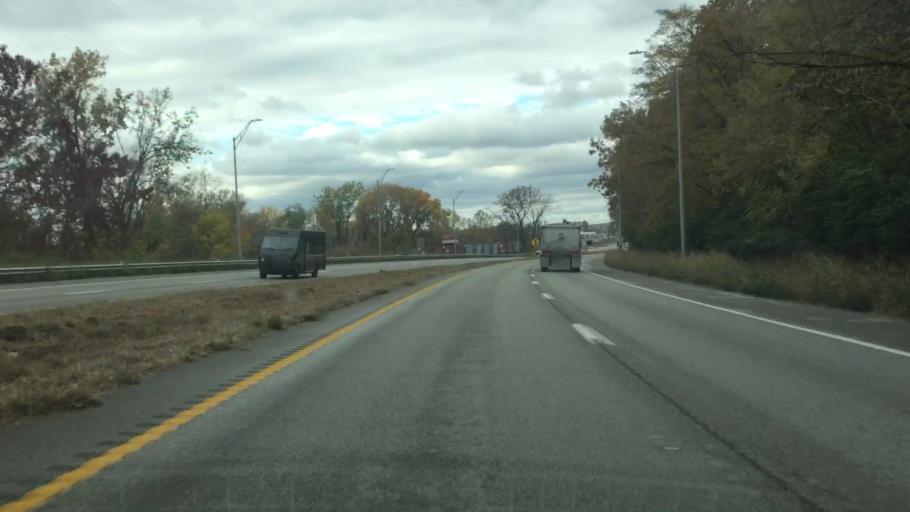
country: US
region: Missouri
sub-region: Clay County
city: North Kansas City
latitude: 39.1477
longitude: -94.5424
